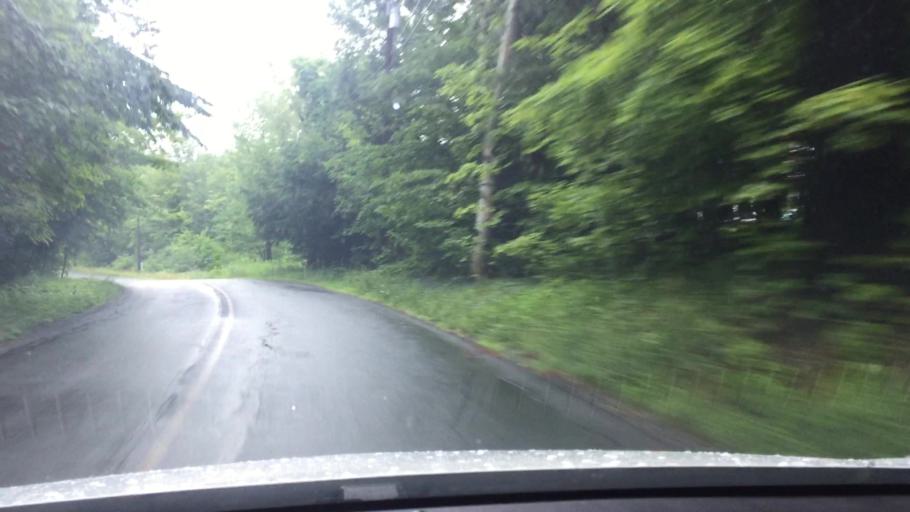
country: US
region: Massachusetts
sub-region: Berkshire County
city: Becket
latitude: 42.2872
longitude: -73.0535
